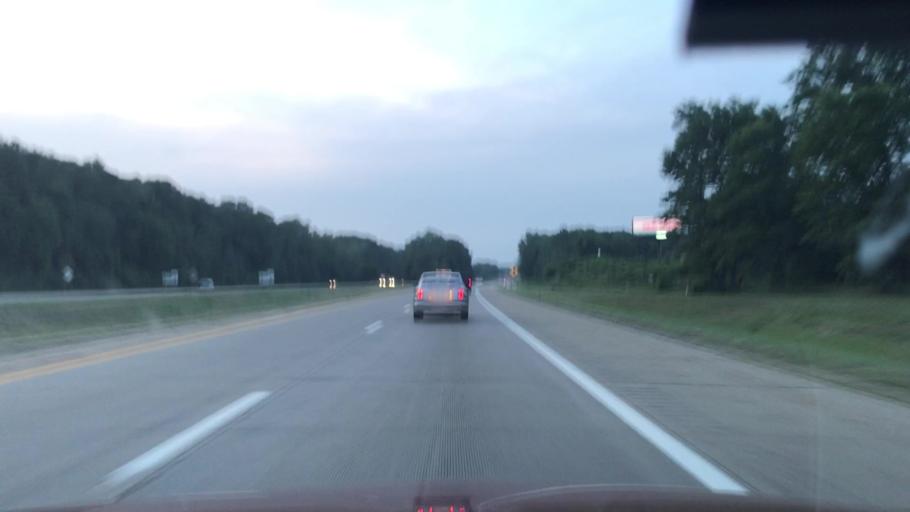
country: US
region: Michigan
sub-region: Kent County
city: Comstock Park
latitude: 43.0460
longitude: -85.6625
